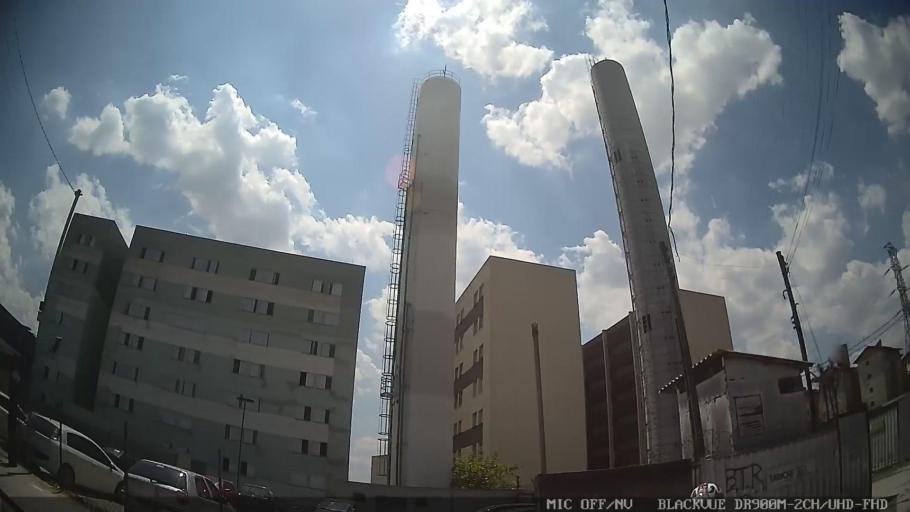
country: BR
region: Sao Paulo
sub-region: Taboao Da Serra
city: Taboao da Serra
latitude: -23.6816
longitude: -46.7967
